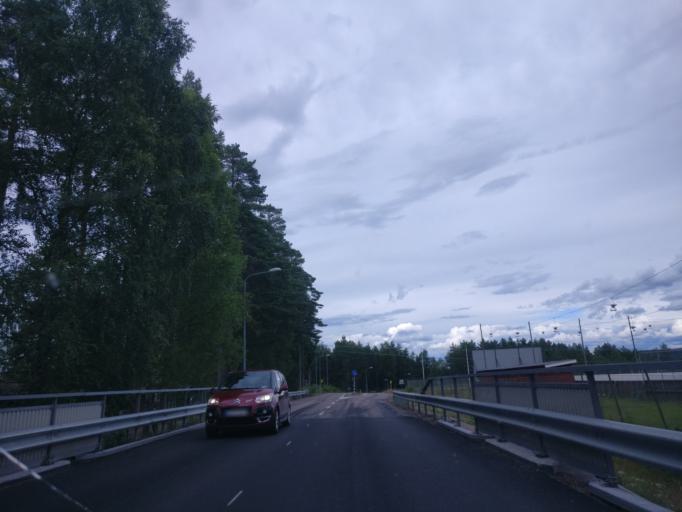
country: SE
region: Vaermland
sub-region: Hagfors Kommun
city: Ekshaerad
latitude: 60.1714
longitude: 13.4848
